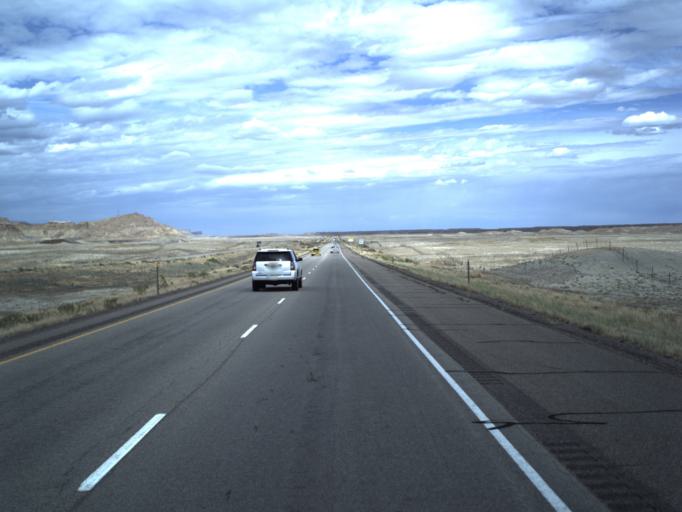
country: US
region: Utah
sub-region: Grand County
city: Moab
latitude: 38.9231
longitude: -109.9213
